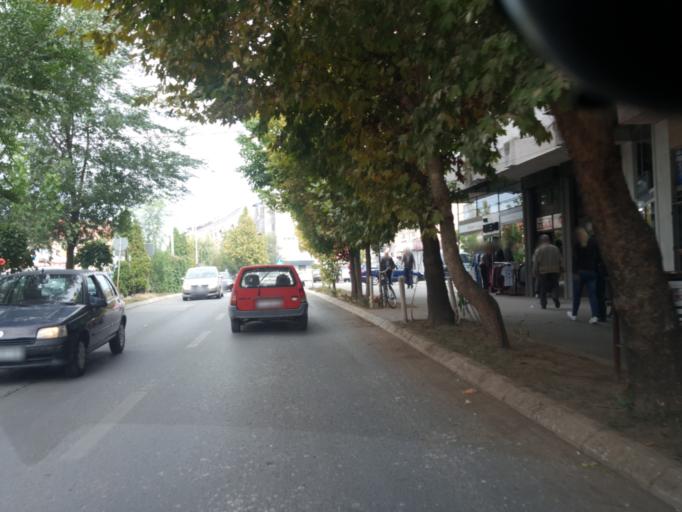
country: XK
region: Gjakova
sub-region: Komuna e Gjakoves
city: Gjakove
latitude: 42.3855
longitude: 20.4280
